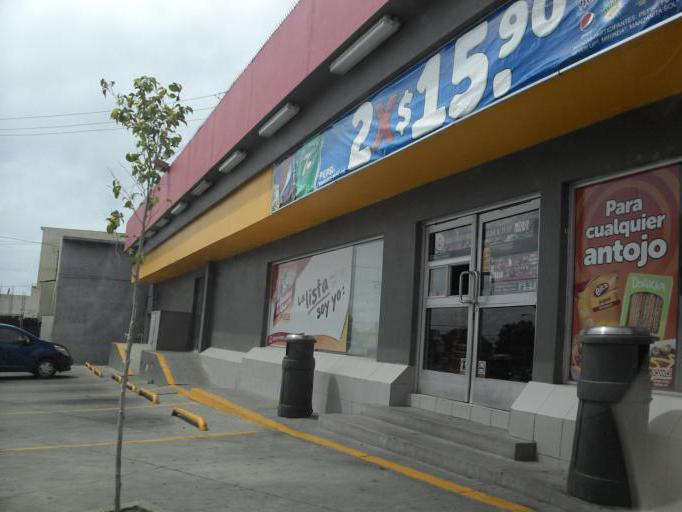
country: MX
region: Baja California
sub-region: Tijuana
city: La Esperanza [Granjas Familiares]
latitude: 32.5093
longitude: -117.1180
